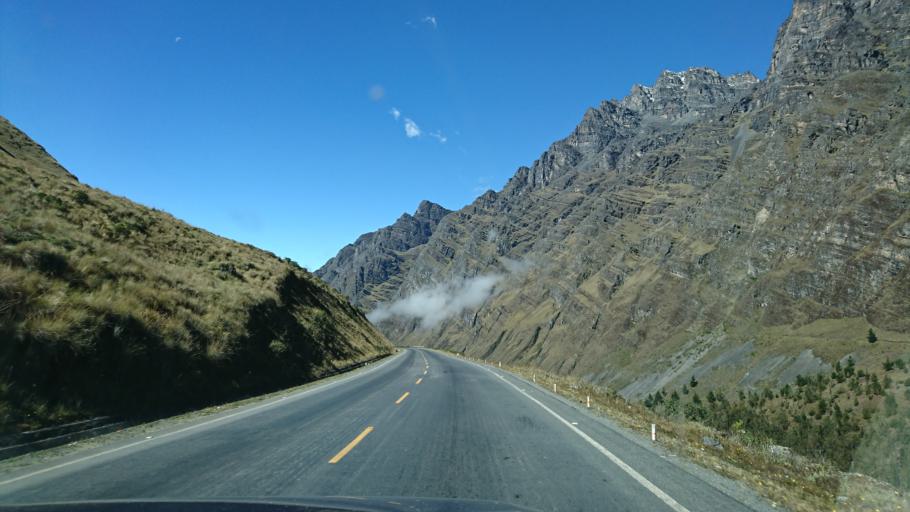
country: BO
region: La Paz
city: La Paz
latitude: -16.3304
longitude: -67.9649
